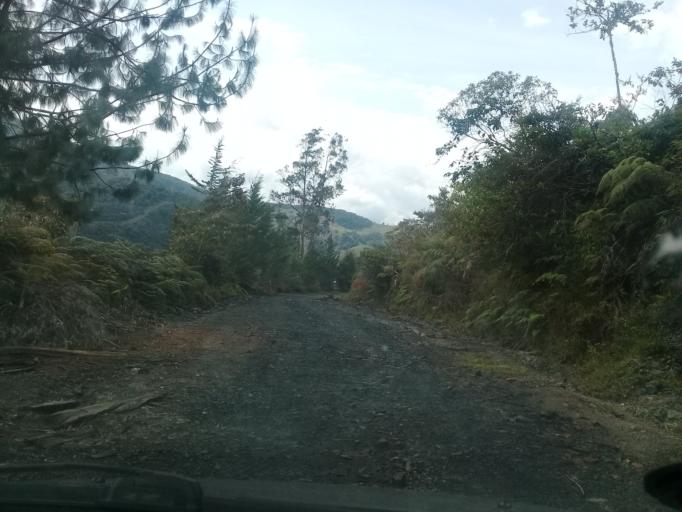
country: CO
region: Cundinamarca
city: Gachala
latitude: 4.7019
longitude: -73.4432
